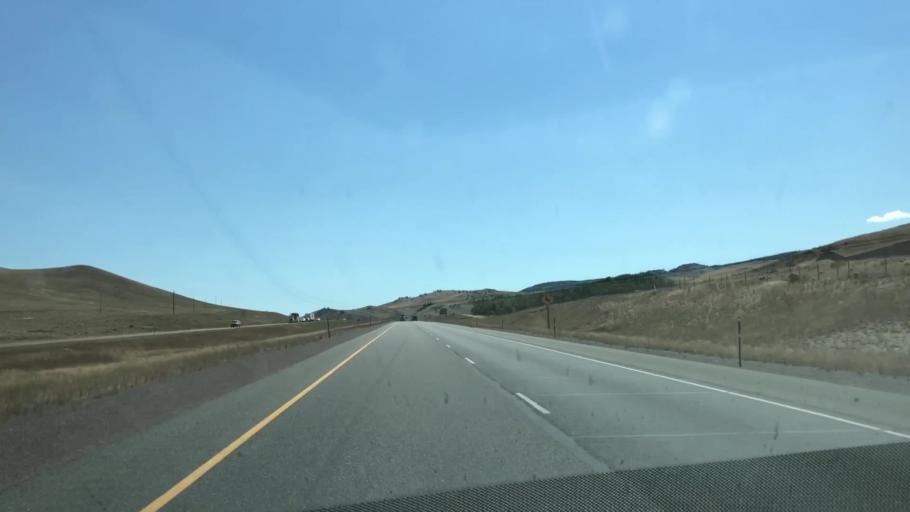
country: US
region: Wyoming
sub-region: Carbon County
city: Saratoga
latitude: 41.6070
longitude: -106.2288
